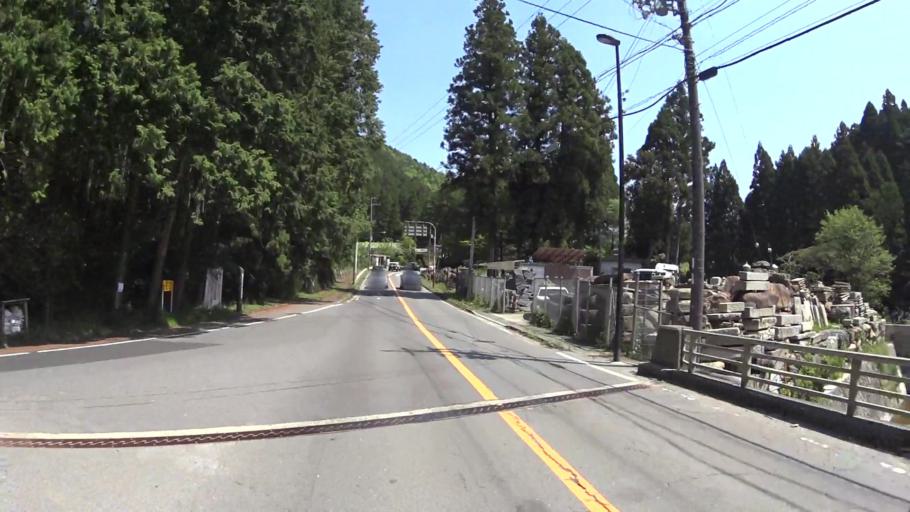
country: JP
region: Shiga Prefecture
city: Kitahama
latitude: 35.1397
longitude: 135.8357
